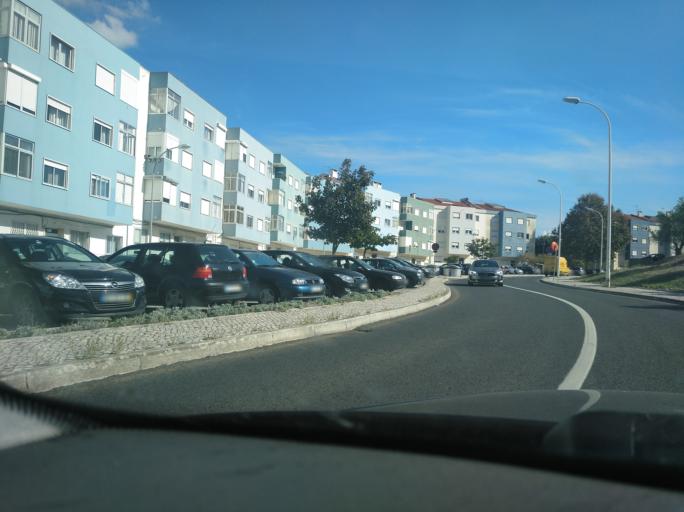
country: PT
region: Lisbon
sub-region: Oeiras
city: Alges
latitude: 38.7068
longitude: -9.2330
